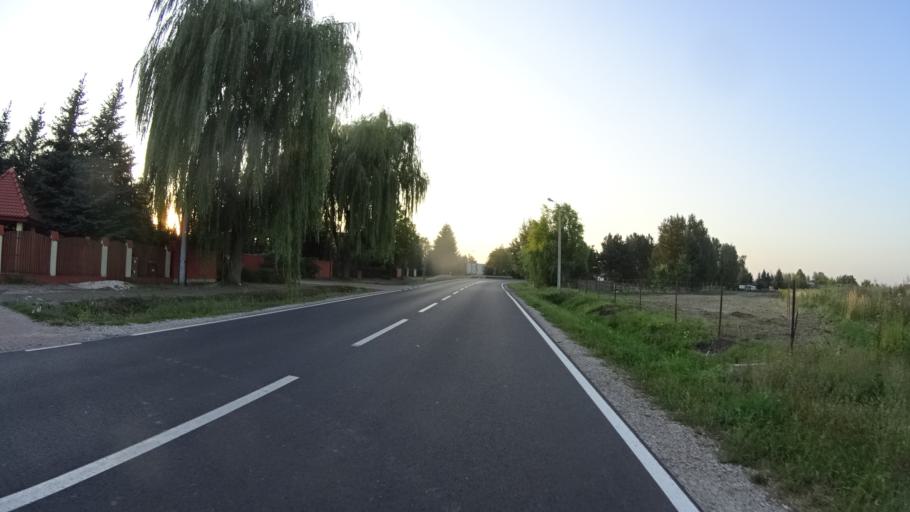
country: PL
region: Masovian Voivodeship
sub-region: Powiat warszawski zachodni
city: Truskaw
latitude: 52.2490
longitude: 20.7424
